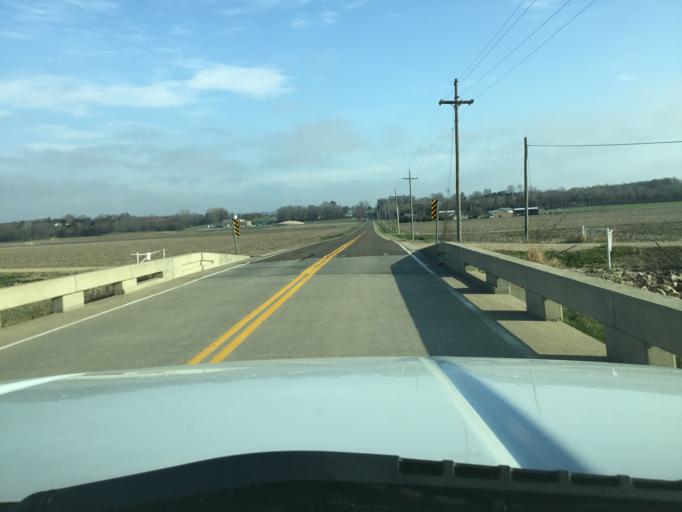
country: US
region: Kansas
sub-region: Shawnee County
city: Topeka
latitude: 39.0979
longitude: -95.7483
